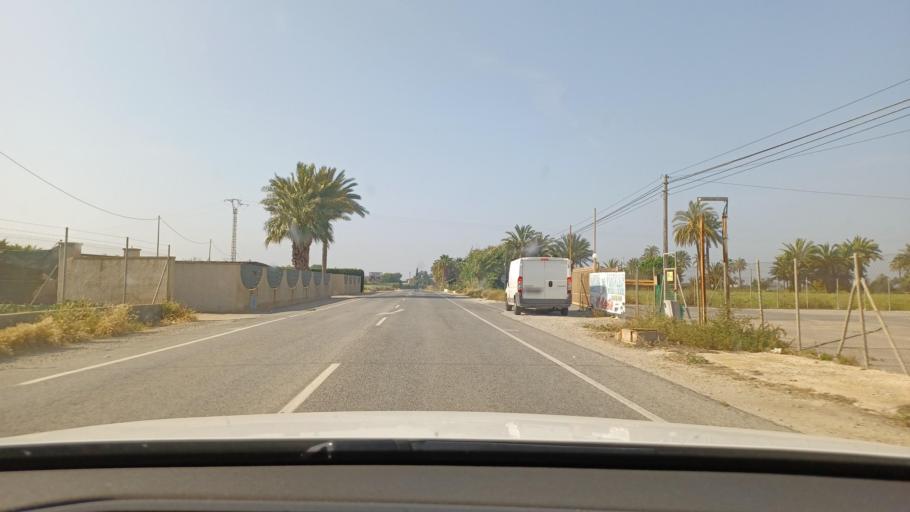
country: ES
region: Valencia
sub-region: Provincia de Alicante
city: Elche
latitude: 38.2300
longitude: -0.7180
